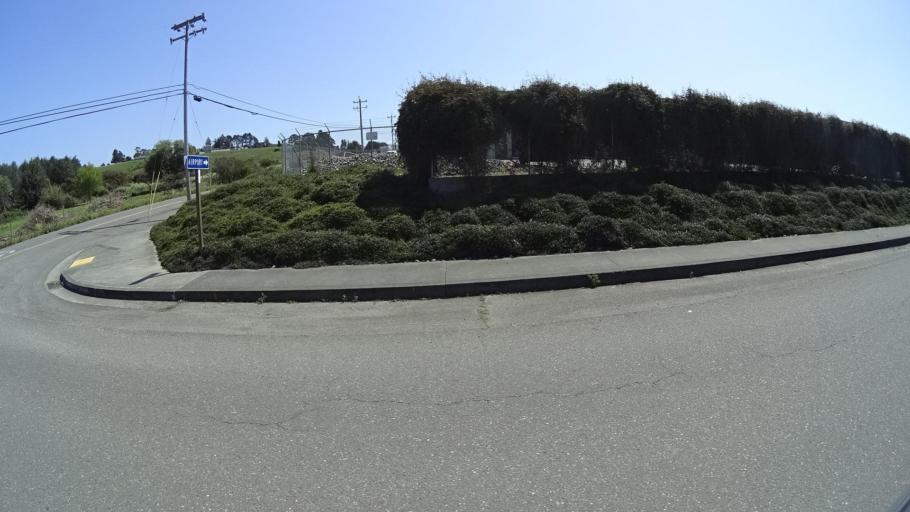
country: US
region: California
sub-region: Humboldt County
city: Hydesville
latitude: 40.5630
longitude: -124.1311
